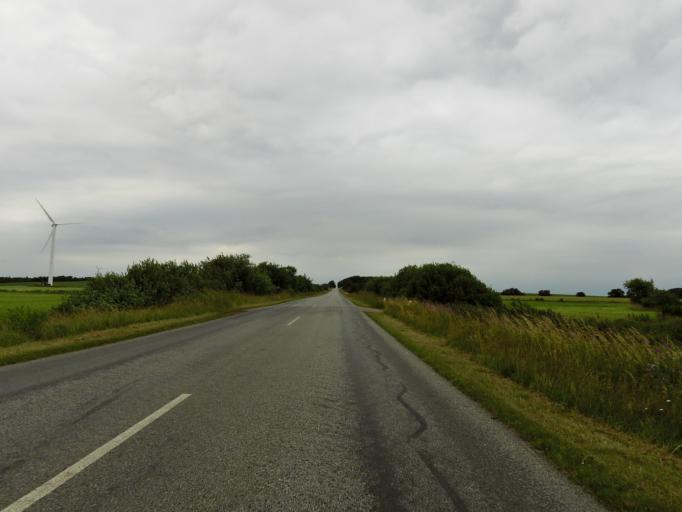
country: DK
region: South Denmark
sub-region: Tonder Kommune
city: Logumkloster
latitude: 55.1319
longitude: 8.9674
